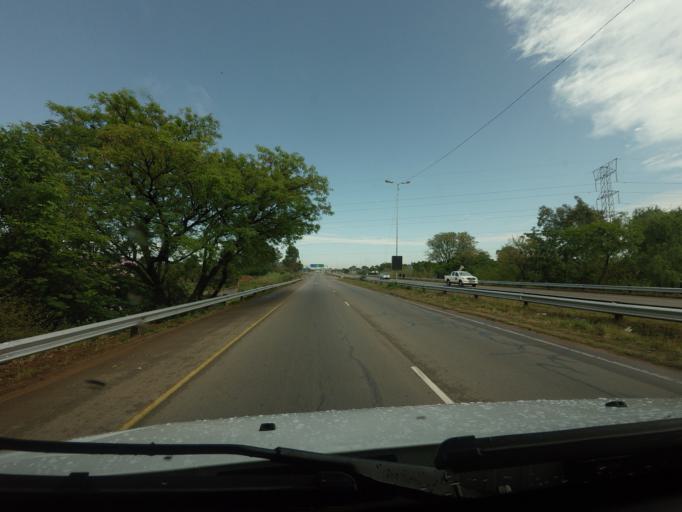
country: ZA
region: Gauteng
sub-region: City of Tshwane Metropolitan Municipality
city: Pretoria
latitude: -25.6855
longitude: 28.2867
